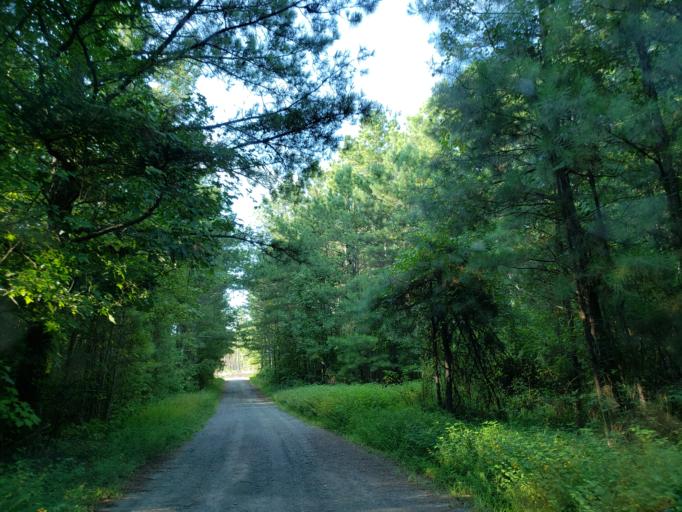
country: US
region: Georgia
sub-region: Bartow County
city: Emerson
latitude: 34.1900
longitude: -84.6490
